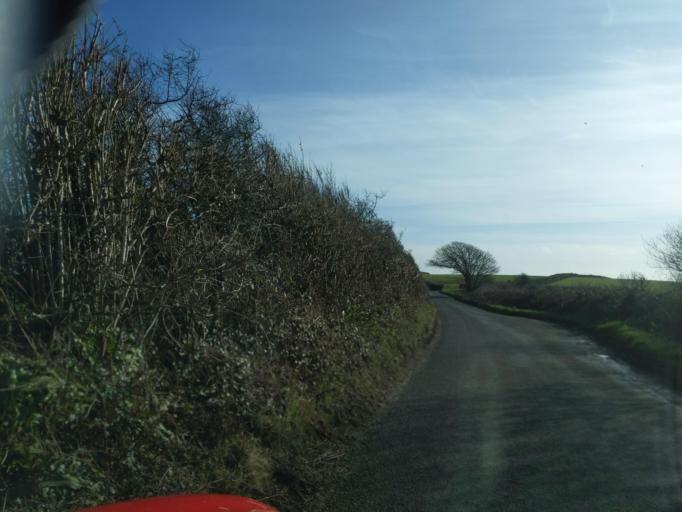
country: GB
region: England
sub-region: Devon
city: Kingsbridge
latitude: 50.3445
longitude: -3.7261
